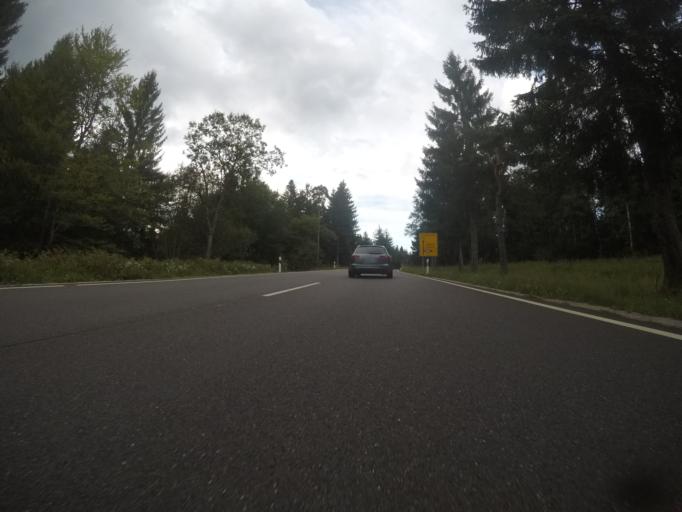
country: DE
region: Baden-Wuerttemberg
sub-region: Freiburg Region
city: Bad Peterstal-Griesbach
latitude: 48.4948
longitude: 8.2506
